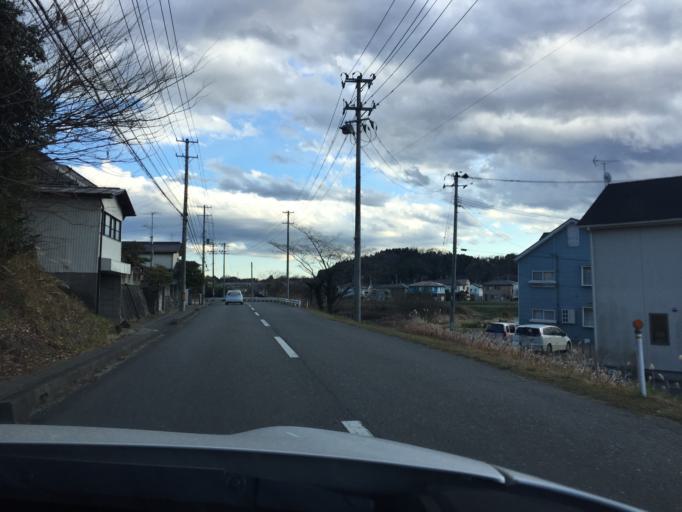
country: JP
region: Fukushima
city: Iwaki
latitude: 37.0641
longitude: 140.8668
